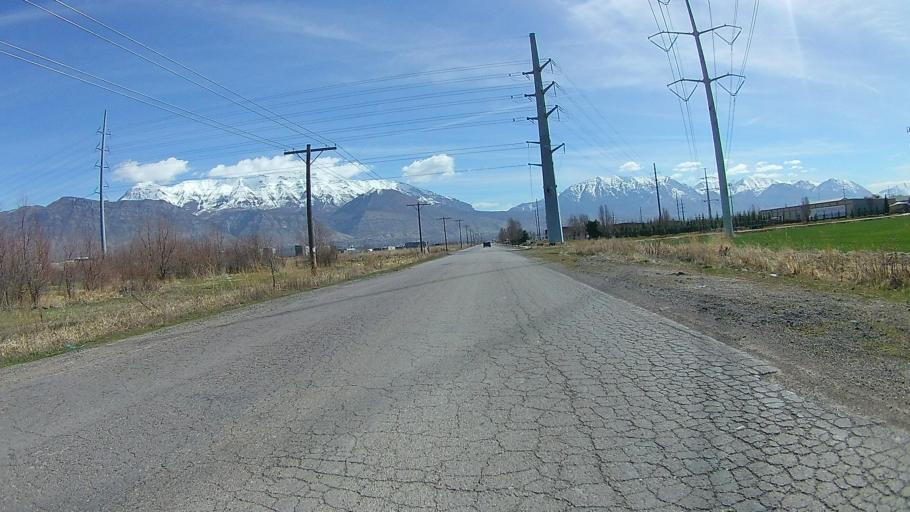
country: US
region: Utah
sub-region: Utah County
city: American Fork
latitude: 40.3477
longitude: -111.7868
